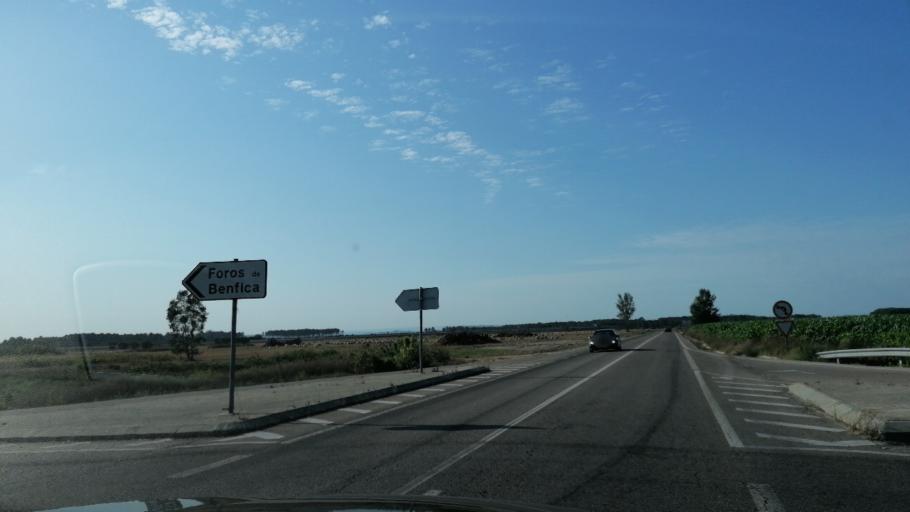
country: PT
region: Santarem
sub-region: Almeirim
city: Fazendas de Almeirim
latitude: 39.1525
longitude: -8.6188
